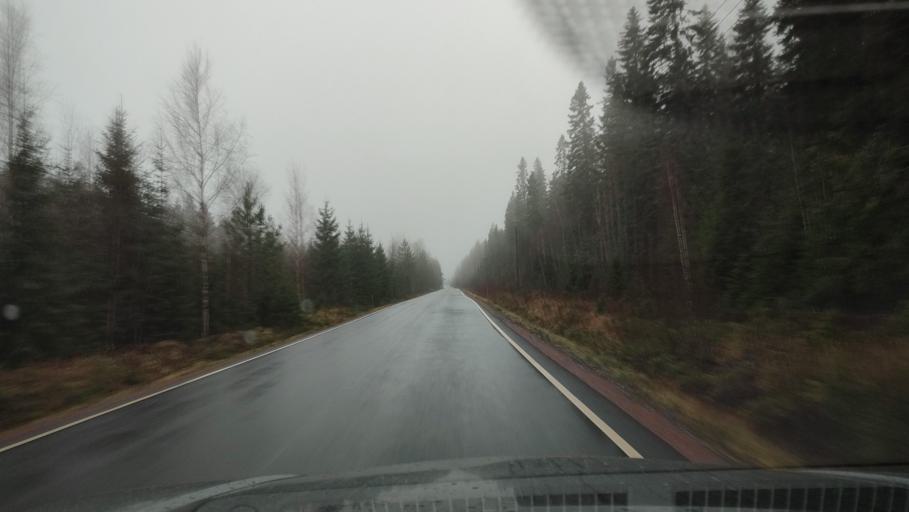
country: FI
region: Southern Ostrobothnia
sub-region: Suupohja
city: Karijoki
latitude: 62.1568
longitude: 21.7185
